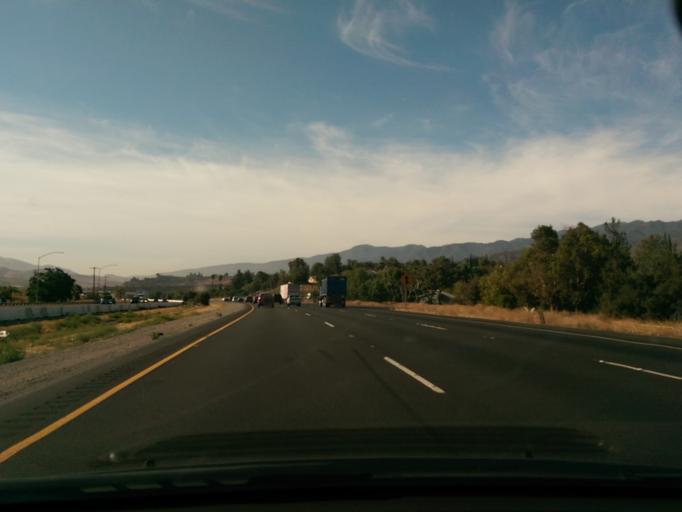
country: US
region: California
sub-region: Riverside County
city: El Cerrito
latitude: 33.8310
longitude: -117.5293
